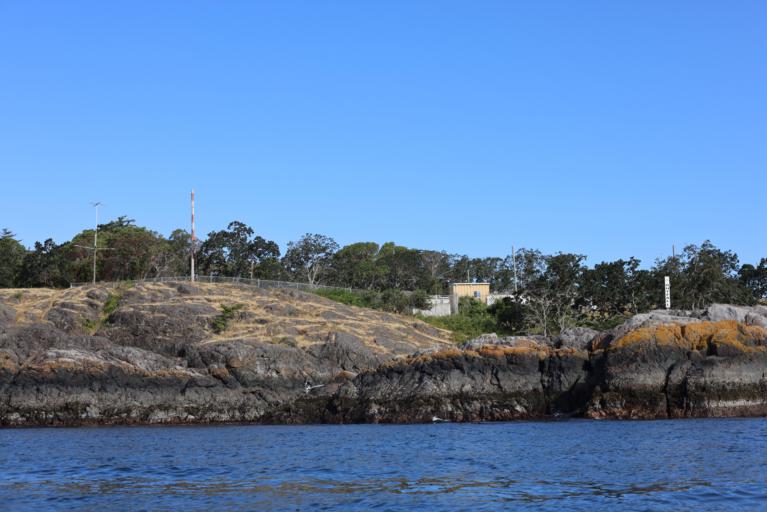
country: CA
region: British Columbia
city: Metchosin
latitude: 48.3404
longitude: -123.5278
